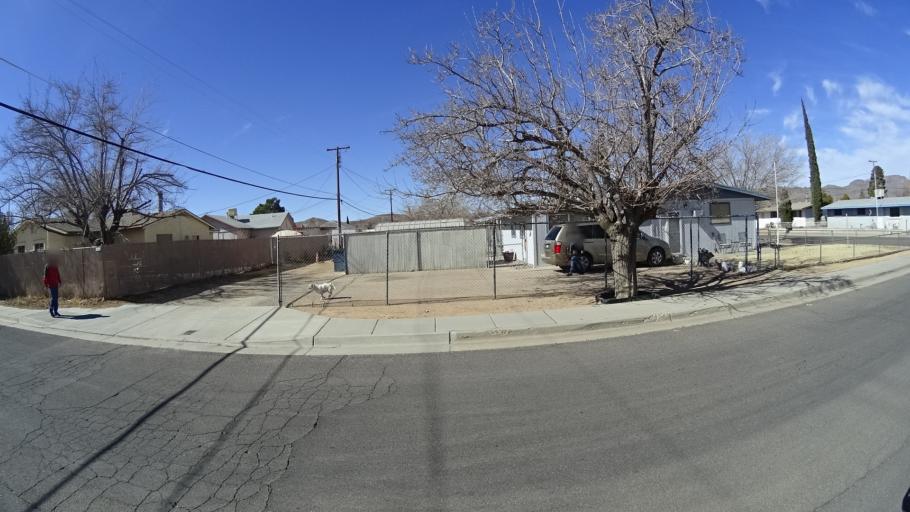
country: US
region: Arizona
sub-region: Mohave County
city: Kingman
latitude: 35.2086
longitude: -114.0291
